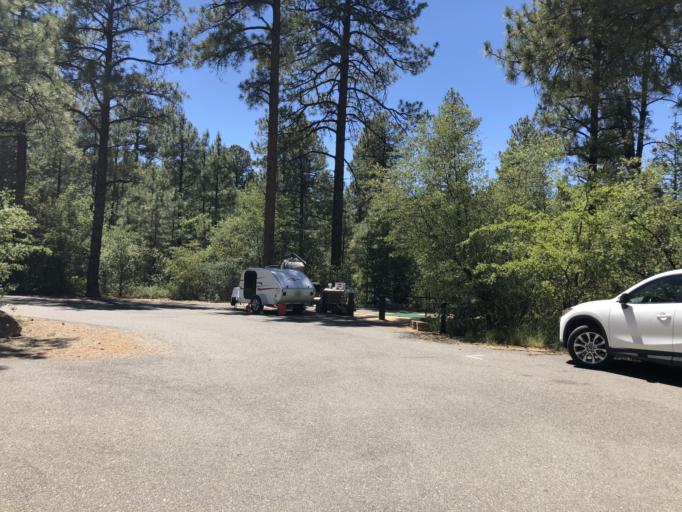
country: US
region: Arizona
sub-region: Yavapai County
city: Prescott
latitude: 34.5180
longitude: -112.3905
